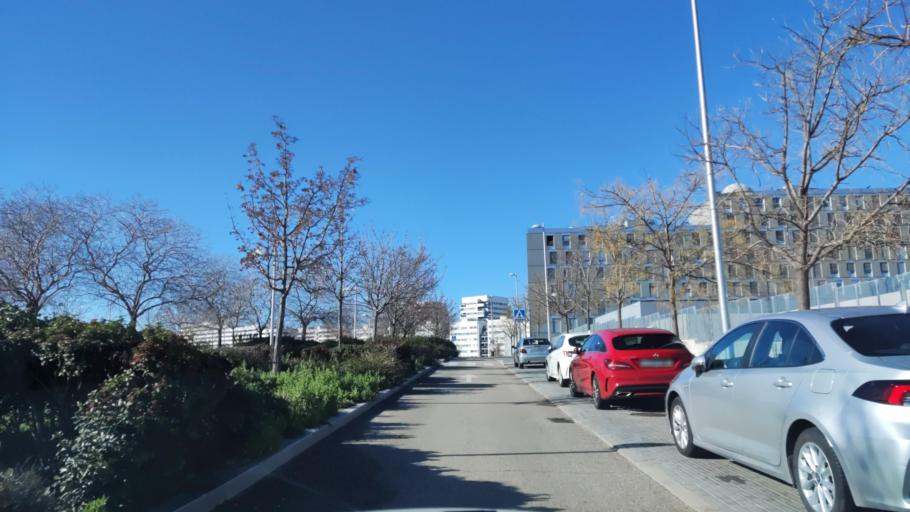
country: ES
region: Madrid
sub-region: Provincia de Madrid
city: Hortaleza
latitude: 40.4863
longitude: -3.6106
